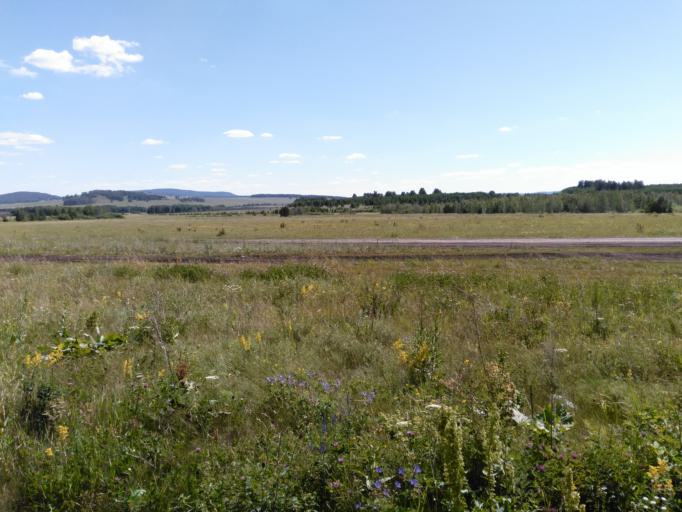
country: RU
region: Bashkortostan
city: Uchaly
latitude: 54.2875
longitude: 59.3557
